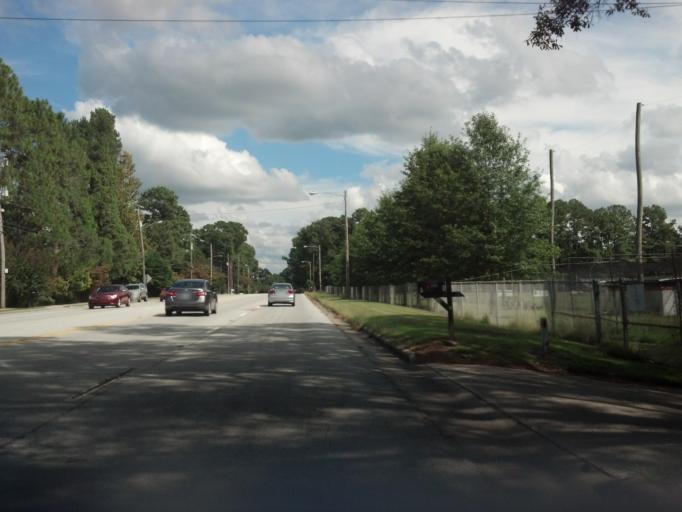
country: US
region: North Carolina
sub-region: Pitt County
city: Greenville
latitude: 35.5897
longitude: -77.3549
